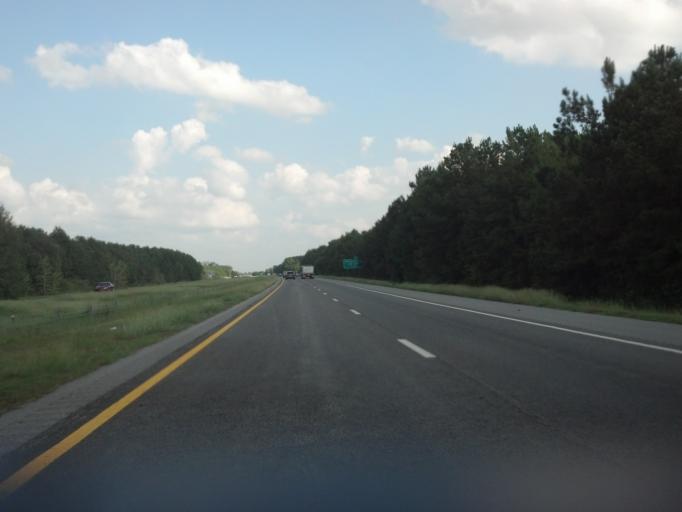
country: US
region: North Carolina
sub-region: Edgecombe County
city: Princeville
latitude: 35.8646
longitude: -77.4839
